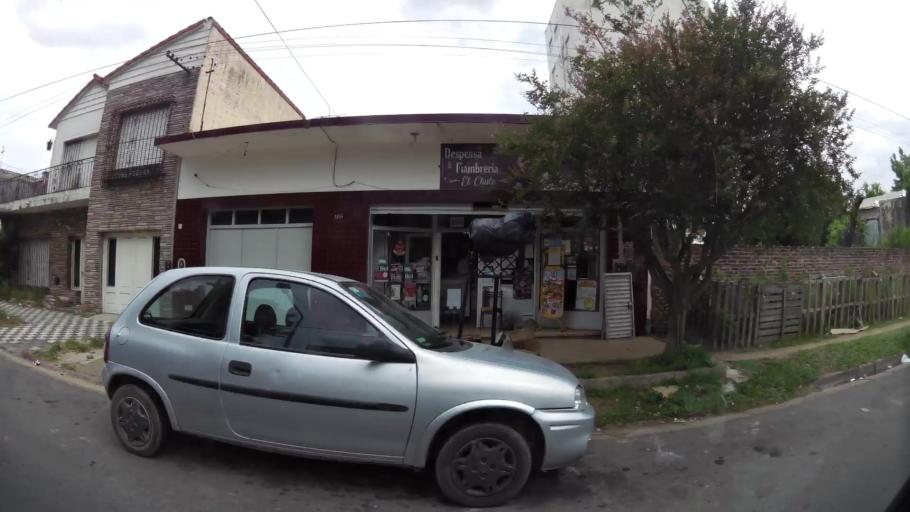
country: AR
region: Buenos Aires
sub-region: Partido de Campana
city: Campana
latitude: -34.1647
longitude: -58.9658
